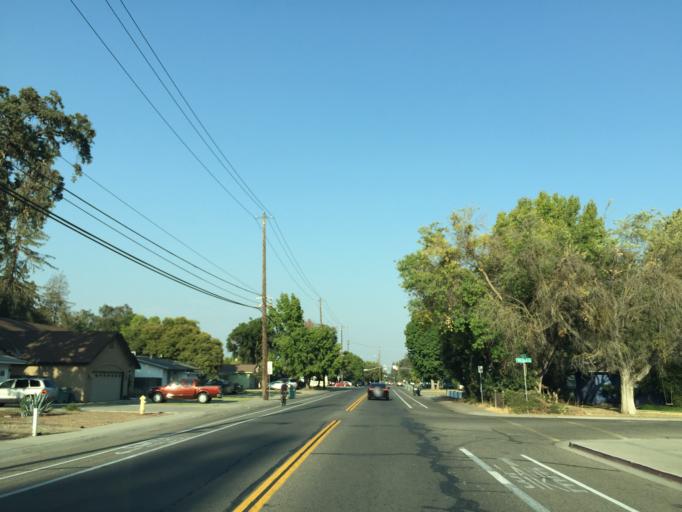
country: US
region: California
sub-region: Tulare County
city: Visalia
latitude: 36.3201
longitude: -119.3080
